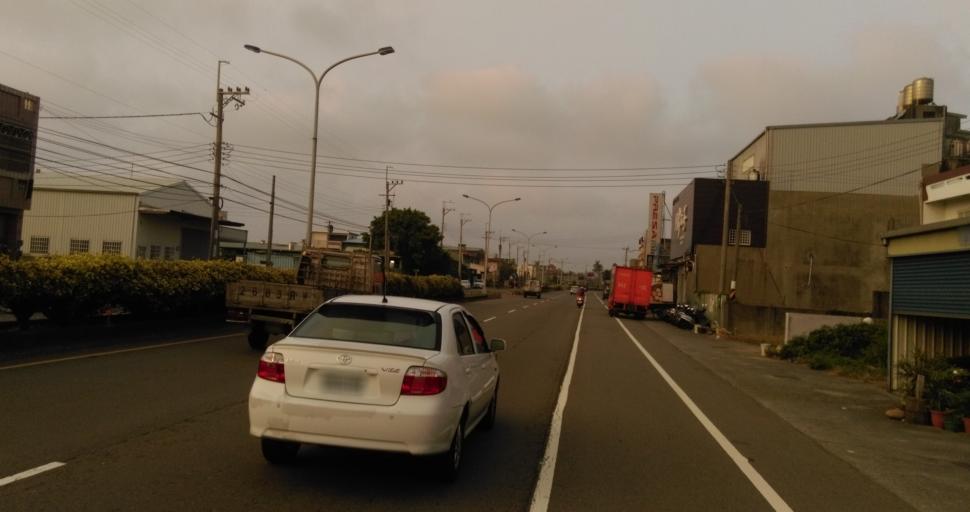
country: TW
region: Taiwan
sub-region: Hsinchu
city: Hsinchu
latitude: 24.8149
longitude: 120.9229
